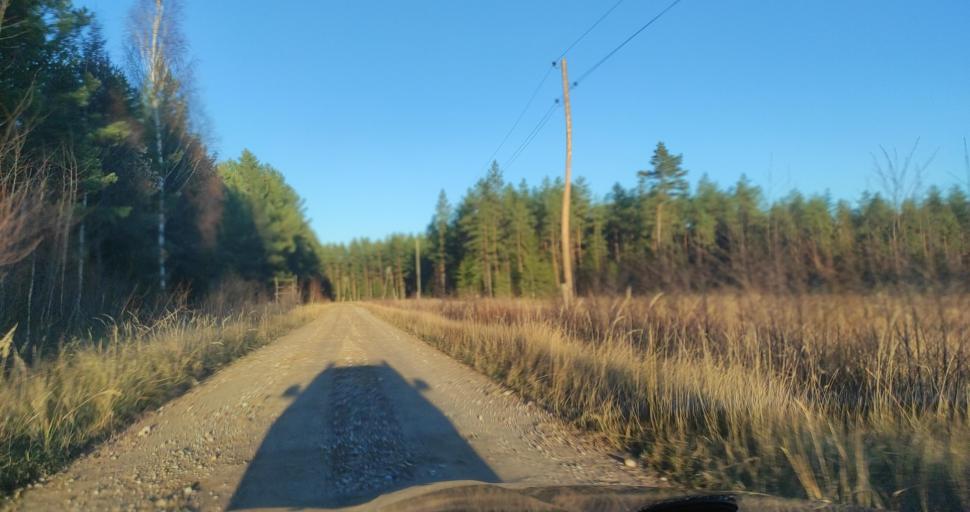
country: LV
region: Dundaga
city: Dundaga
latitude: 57.3716
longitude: 22.0753
